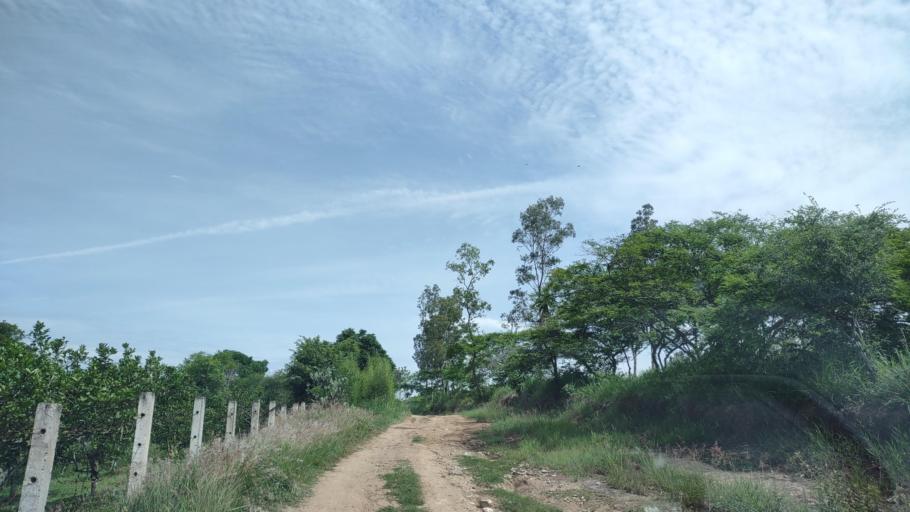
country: MX
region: Veracruz
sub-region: Emiliano Zapata
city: Dos Rios
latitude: 19.4713
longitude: -96.8294
